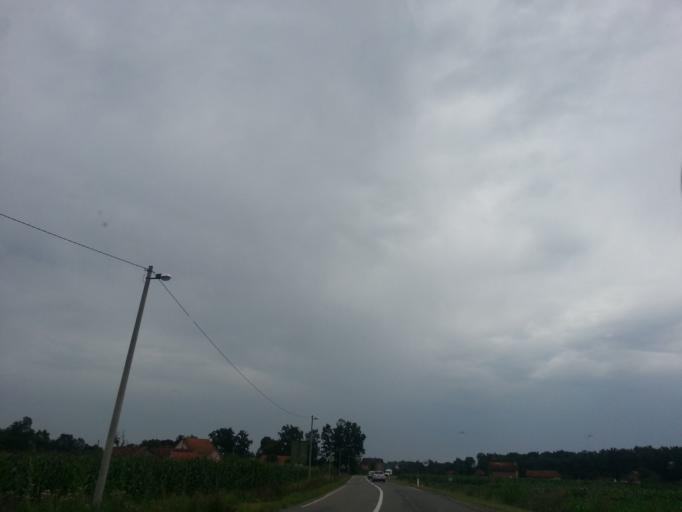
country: BA
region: Republika Srpska
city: Velika Obarska
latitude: 44.8222
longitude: 19.0454
